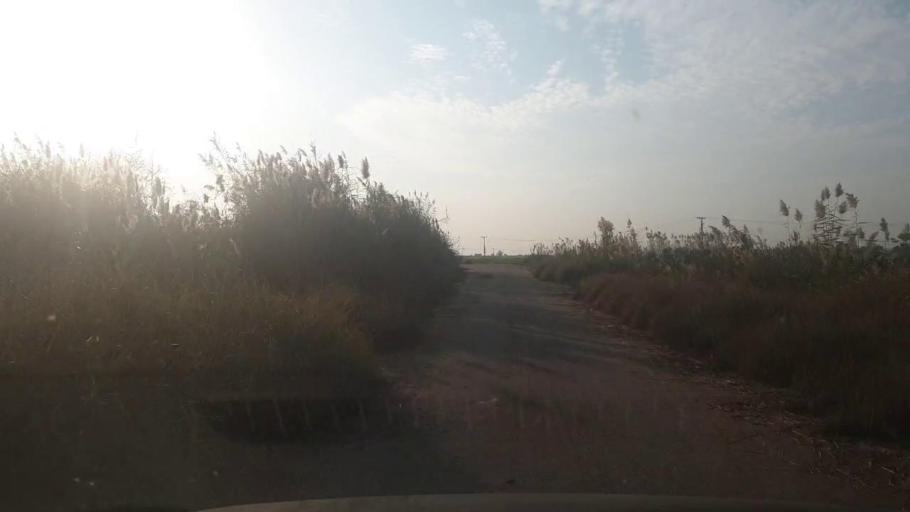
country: PK
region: Sindh
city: Sakrand
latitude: 26.0775
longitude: 68.4004
